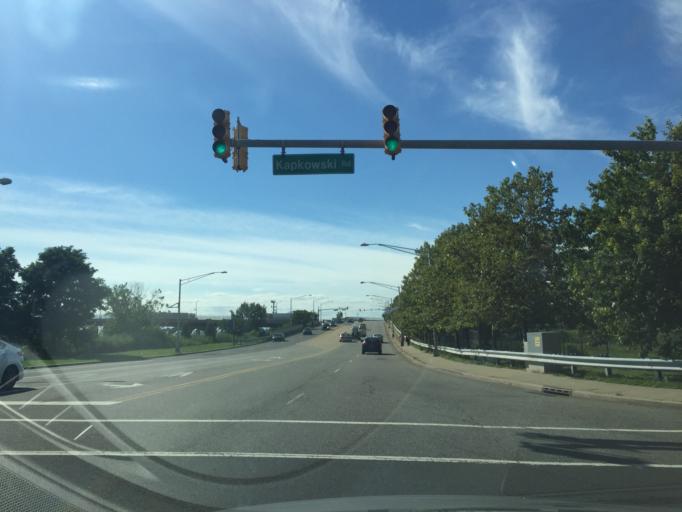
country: US
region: New Jersey
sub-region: Union County
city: Elizabeth
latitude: 40.6604
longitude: -74.1765
